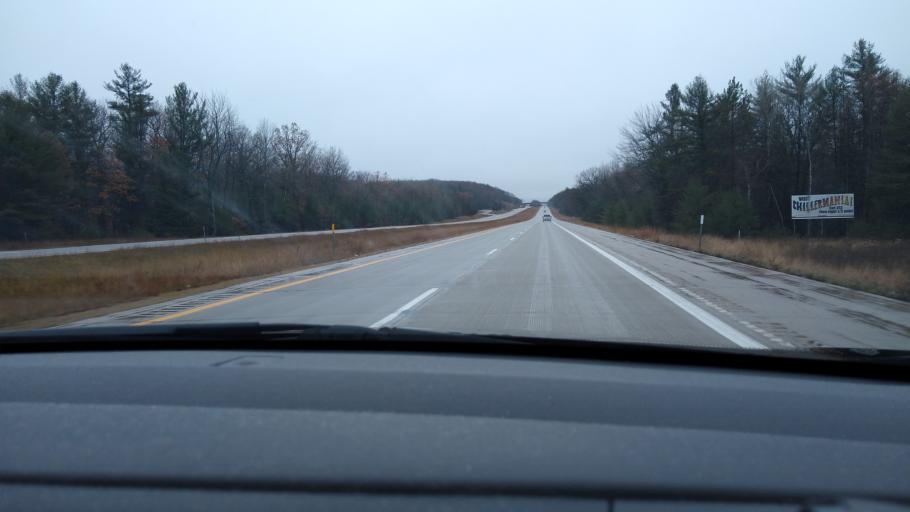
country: US
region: Michigan
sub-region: Cheboygan County
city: Indian River
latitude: 45.5103
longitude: -84.6159
